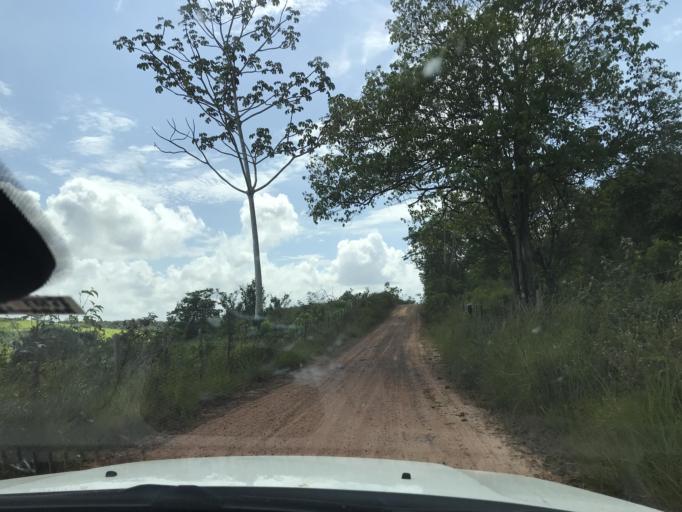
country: BR
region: Bahia
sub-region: Entre Rios
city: Entre Rios
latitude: -12.1786
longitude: -38.0615
